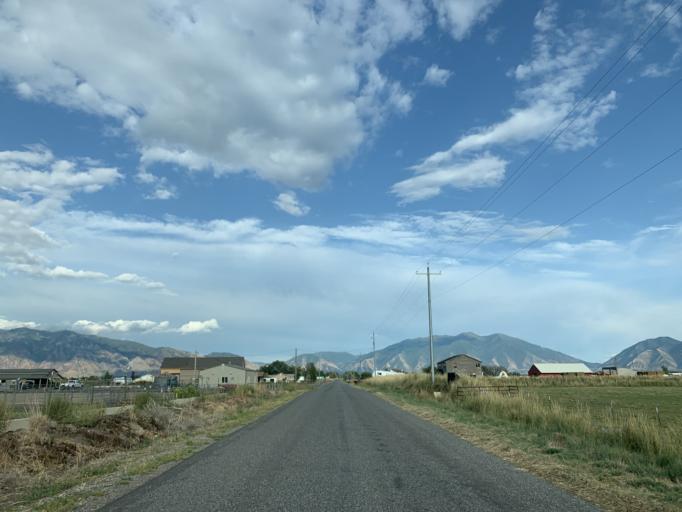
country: US
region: Utah
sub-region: Utah County
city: Benjamin
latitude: 40.1288
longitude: -111.7656
